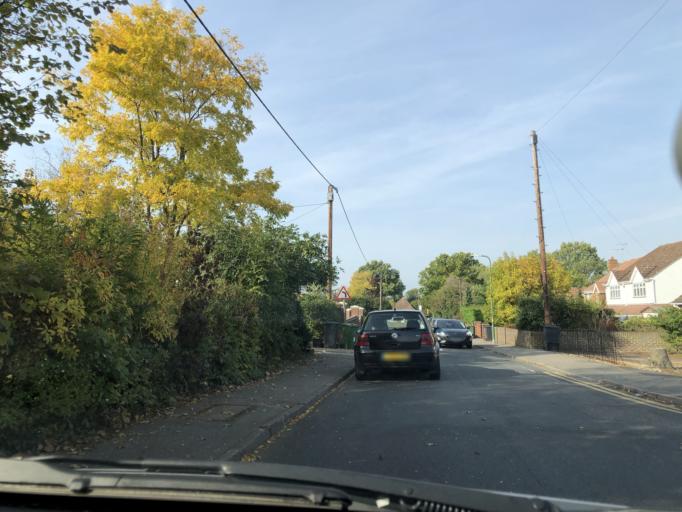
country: GB
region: England
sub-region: Kent
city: Swanley
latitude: 51.4253
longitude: 0.1756
